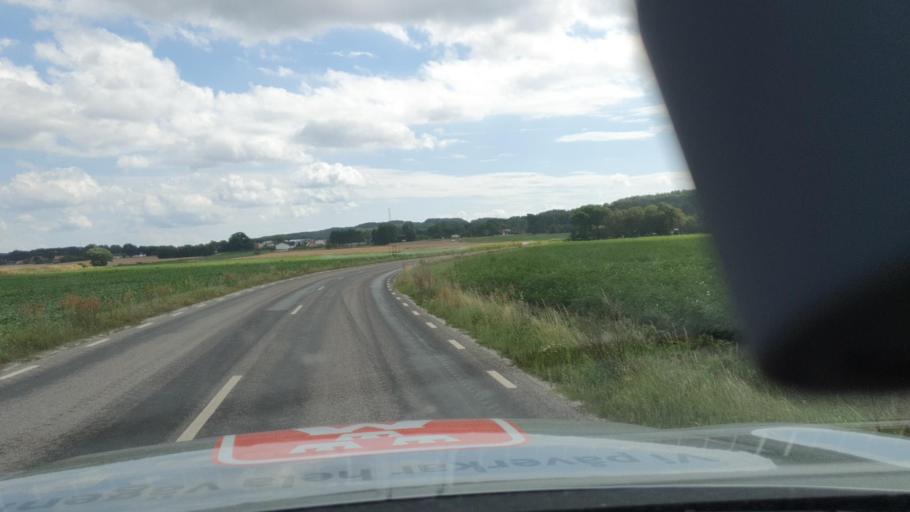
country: SE
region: Blekinge
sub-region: Karlshamns Kommun
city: Morrum
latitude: 56.0383
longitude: 14.7233
